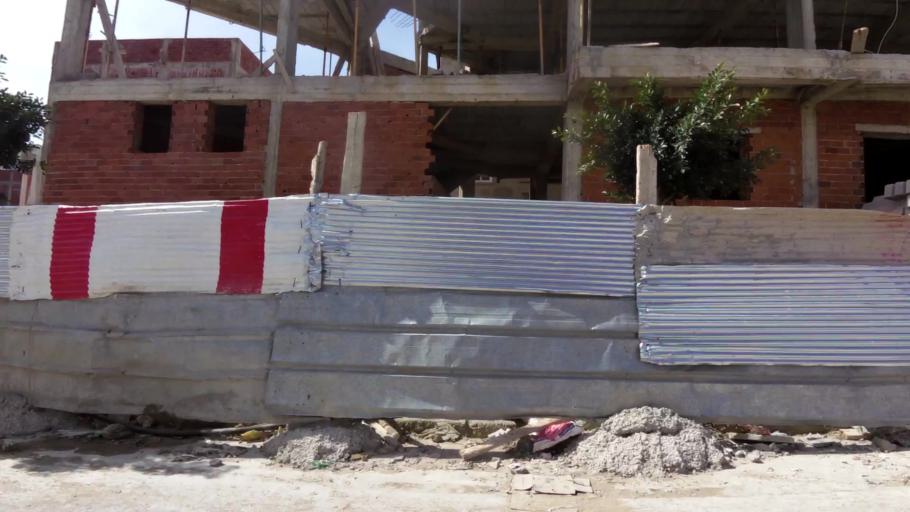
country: MA
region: Tanger-Tetouan
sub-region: Tanger-Assilah
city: Tangier
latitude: 35.7327
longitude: -5.8037
